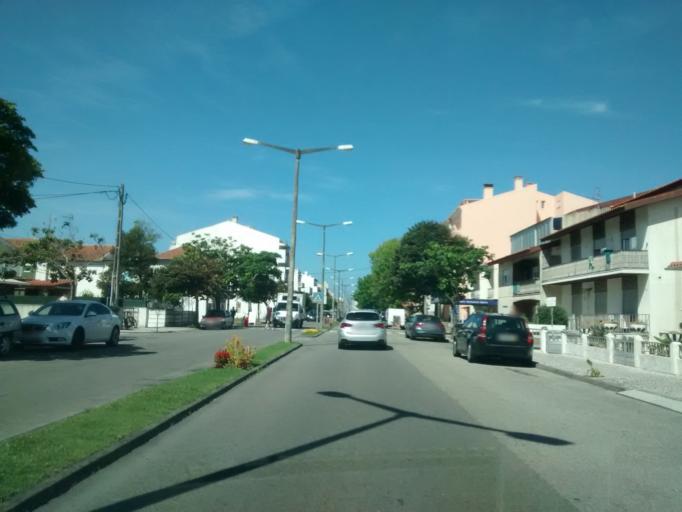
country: PT
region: Coimbra
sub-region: Mira
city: Mira
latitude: 40.4557
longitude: -8.7931
